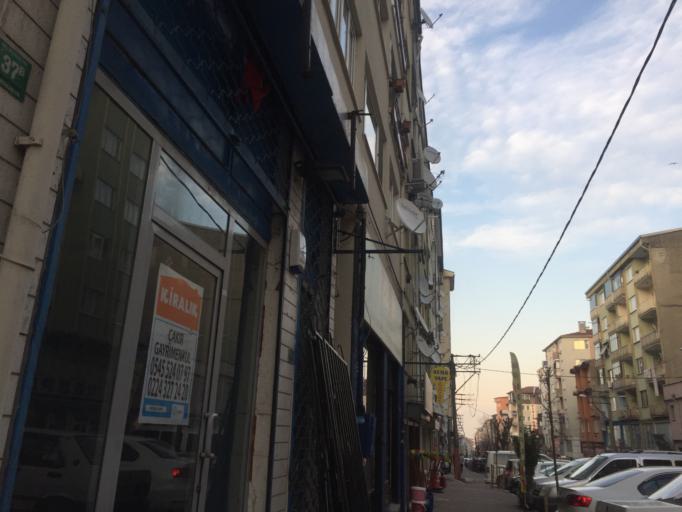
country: TR
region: Bursa
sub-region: Osmangazi
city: Bursa
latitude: 40.1860
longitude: 29.0766
